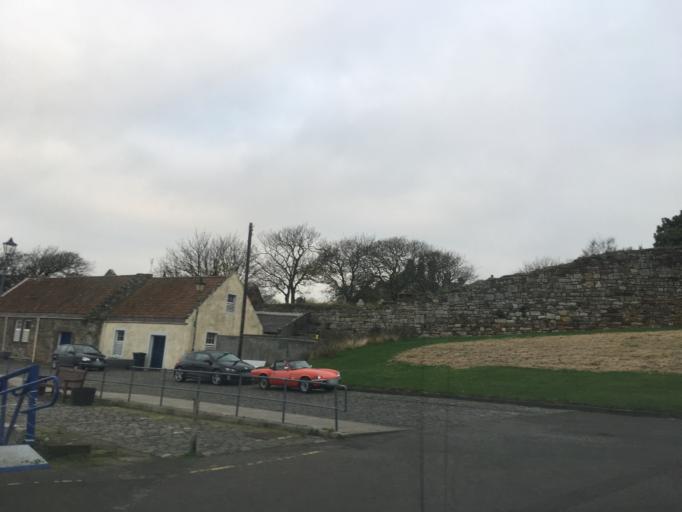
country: GB
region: Scotland
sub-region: Fife
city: Saint Andrews
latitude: 56.3391
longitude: -2.7844
